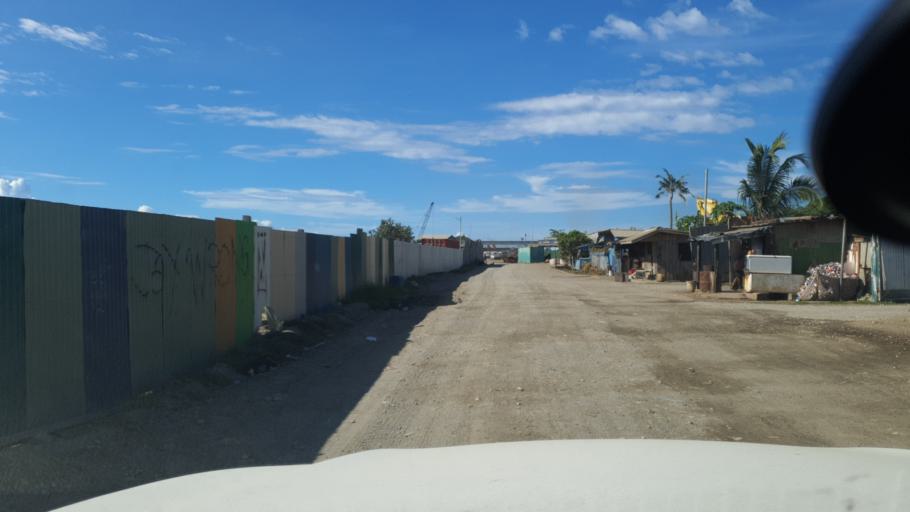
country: SB
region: Guadalcanal
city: Honiara
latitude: -9.4237
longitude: 160.0073
